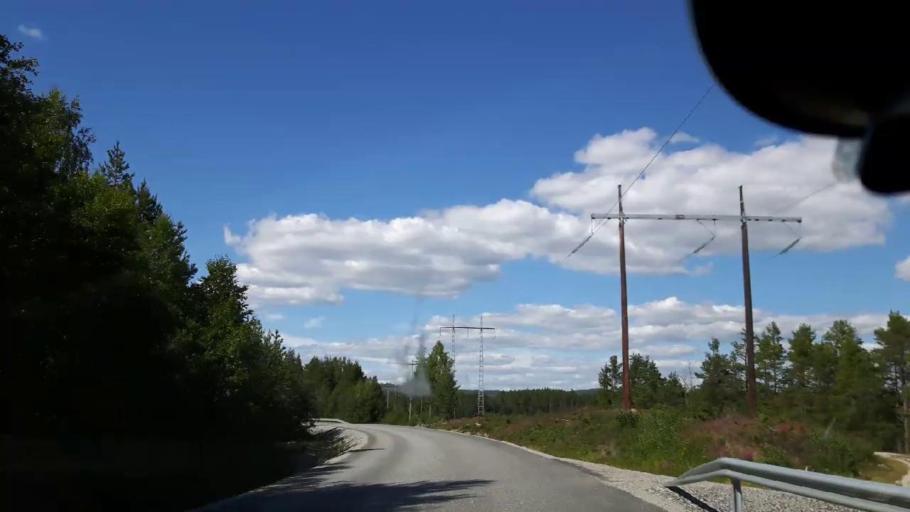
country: SE
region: Vaesternorrland
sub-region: Ange Kommun
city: Fransta
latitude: 62.6913
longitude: 16.3954
